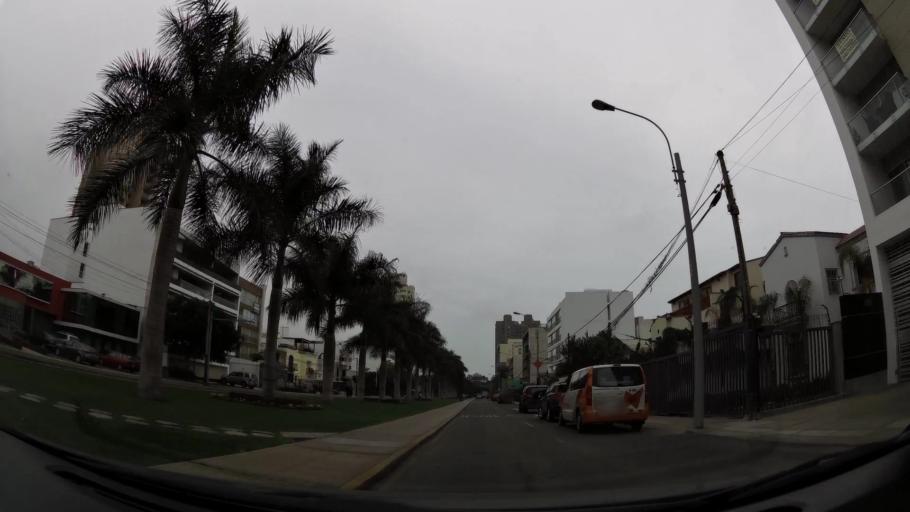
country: PE
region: Lima
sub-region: Lima
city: San Isidro
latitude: -12.0952
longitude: -77.0506
